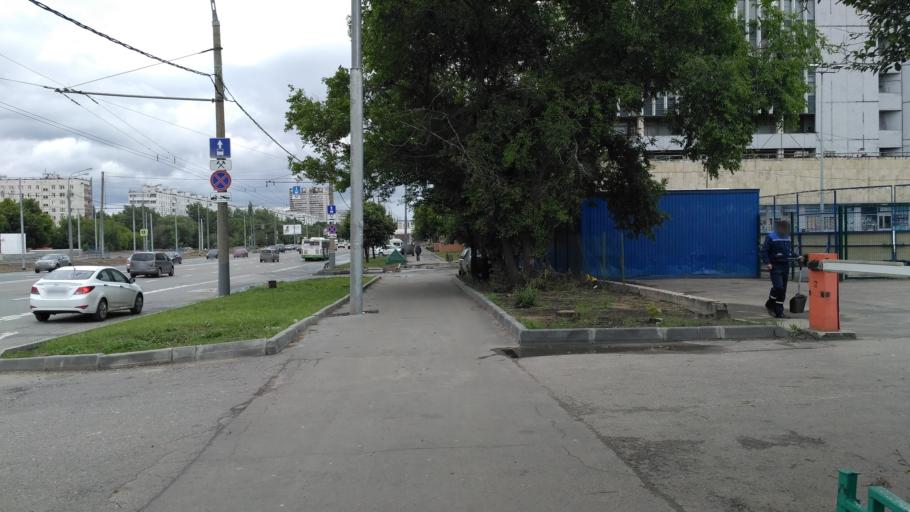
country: RU
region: Moscow
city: Metrogorodok
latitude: 55.8031
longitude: 37.7558
